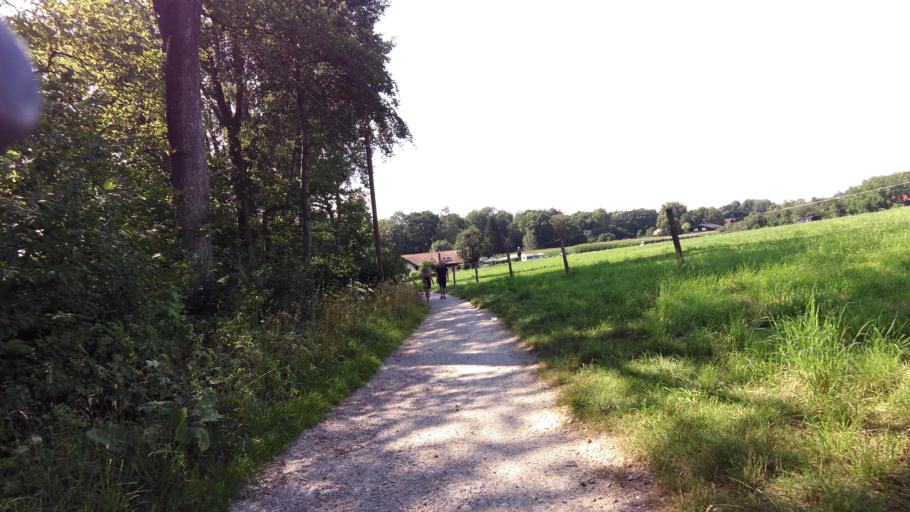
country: DE
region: Bavaria
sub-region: Upper Bavaria
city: Chieming
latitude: 47.9018
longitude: 12.5220
